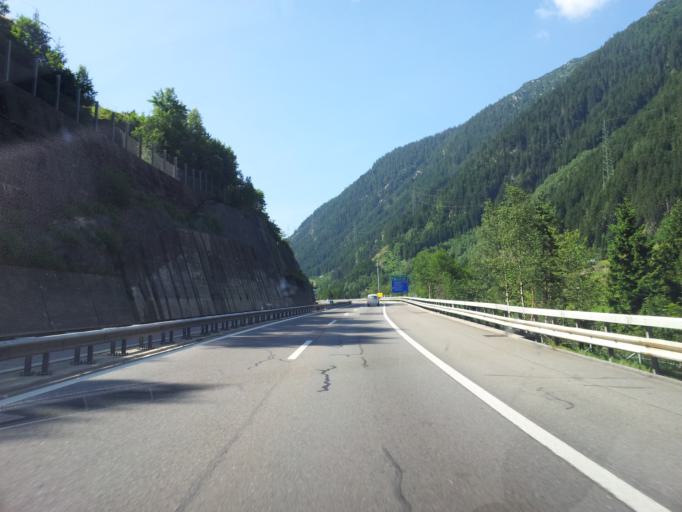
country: CH
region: Uri
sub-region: Uri
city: Andermatt
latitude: 46.6944
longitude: 8.5966
